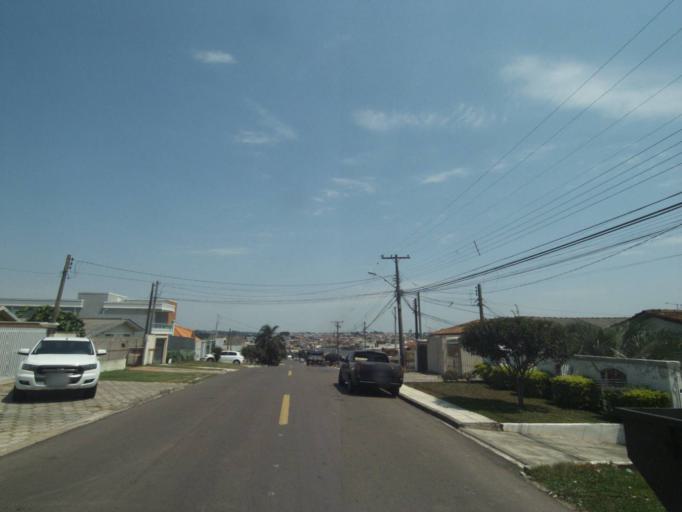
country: BR
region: Parana
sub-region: Sao Jose Dos Pinhais
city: Sao Jose dos Pinhais
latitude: -25.5178
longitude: -49.2641
